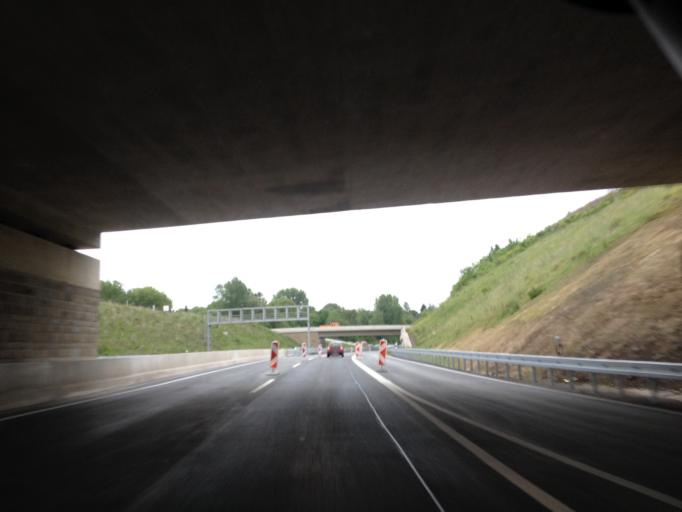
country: DE
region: North Rhine-Westphalia
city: Bochum-Hordel
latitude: 51.4808
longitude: 7.1802
